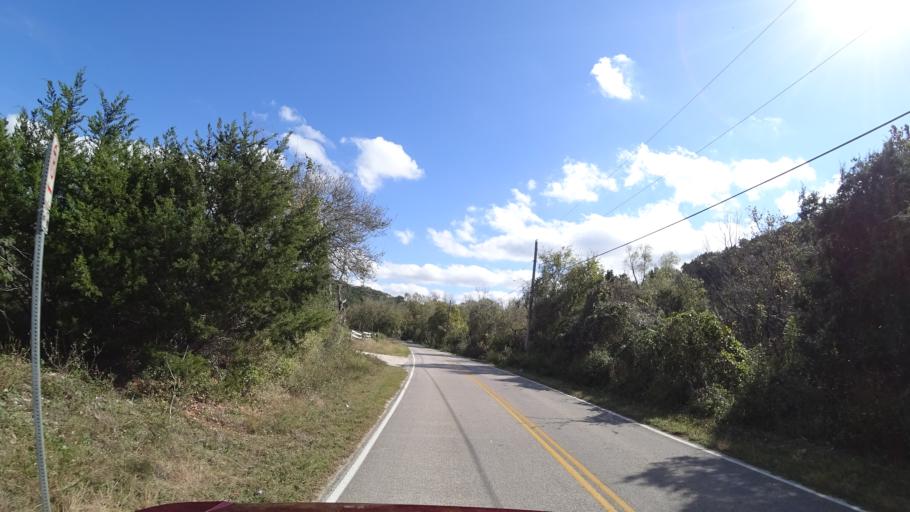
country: US
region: Texas
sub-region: Williamson County
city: Jollyville
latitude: 30.3981
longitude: -97.7815
